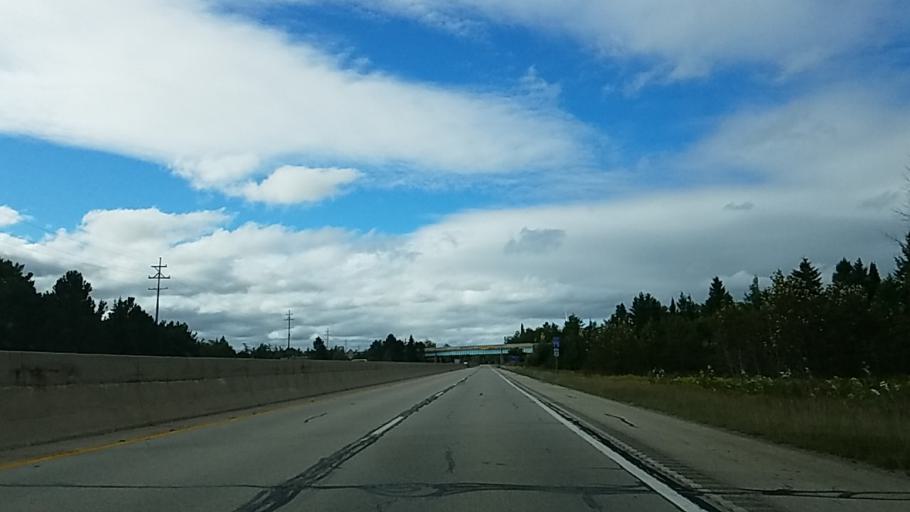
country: US
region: Michigan
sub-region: Mackinac County
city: Saint Ignace
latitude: 45.7748
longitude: -84.7342
